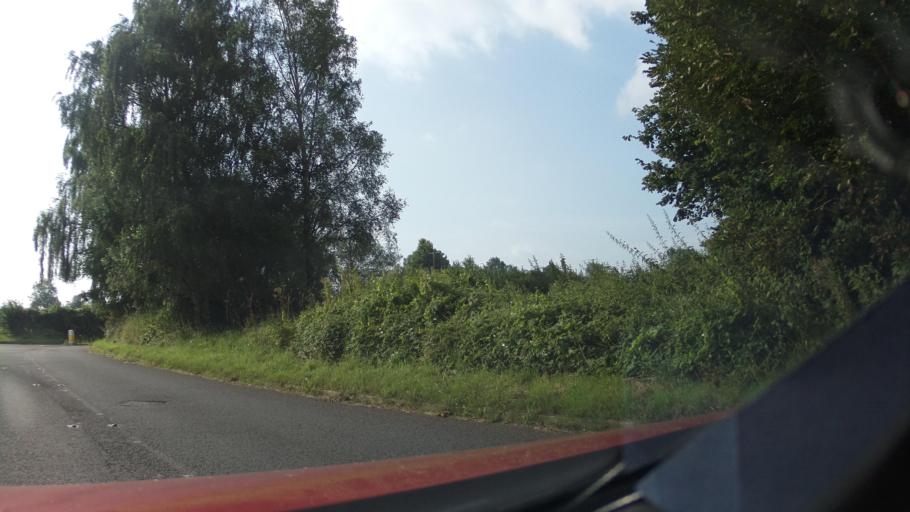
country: GB
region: England
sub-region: Bath and North East Somerset
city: Chew Magna
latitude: 51.3675
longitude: -2.6317
